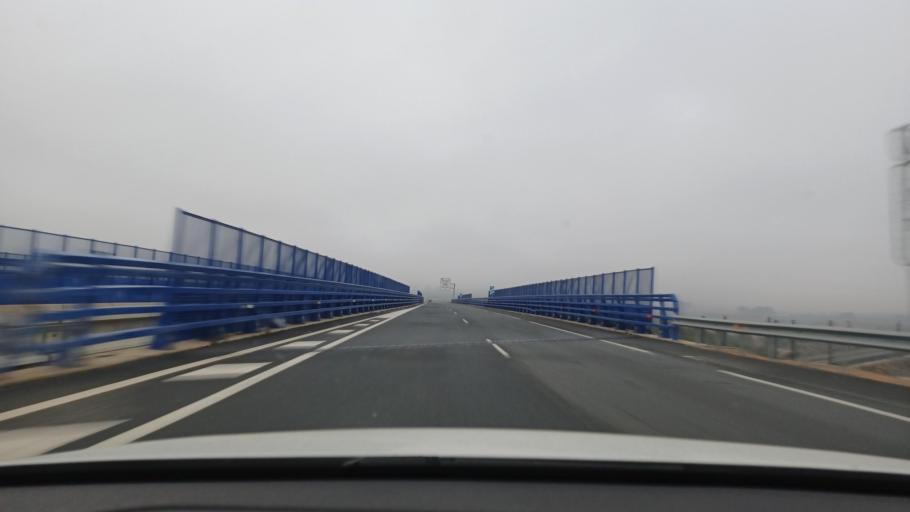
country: ES
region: Valencia
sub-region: Provincia de Valencia
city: La Font de la Figuera
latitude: 38.7909
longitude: -0.8925
